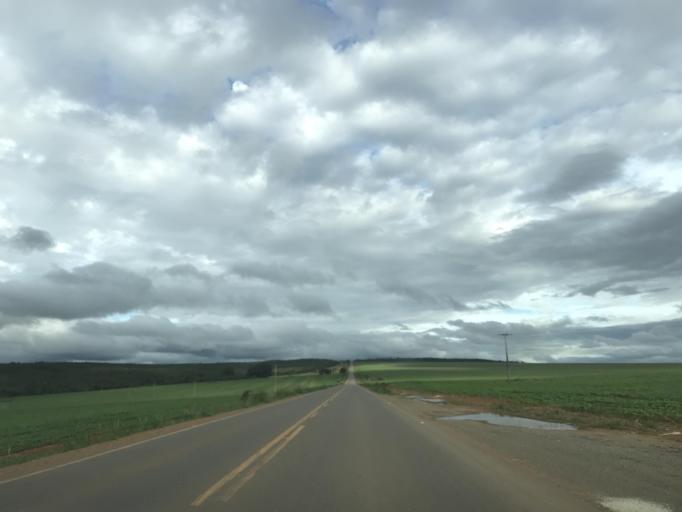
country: BR
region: Goias
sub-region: Vianopolis
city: Vianopolis
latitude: -16.5764
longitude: -48.3214
